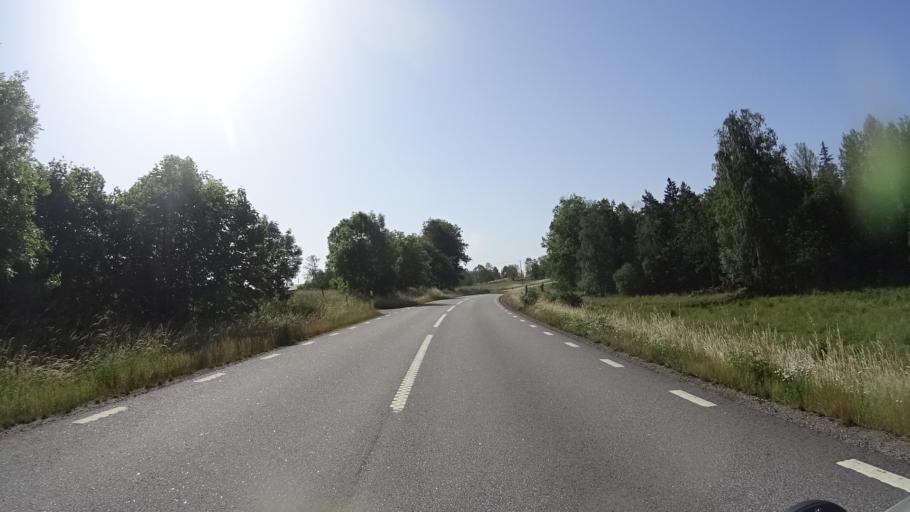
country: SE
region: OEstergoetland
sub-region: Atvidabergs Kommun
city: Atvidaberg
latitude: 58.1399
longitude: 16.0863
